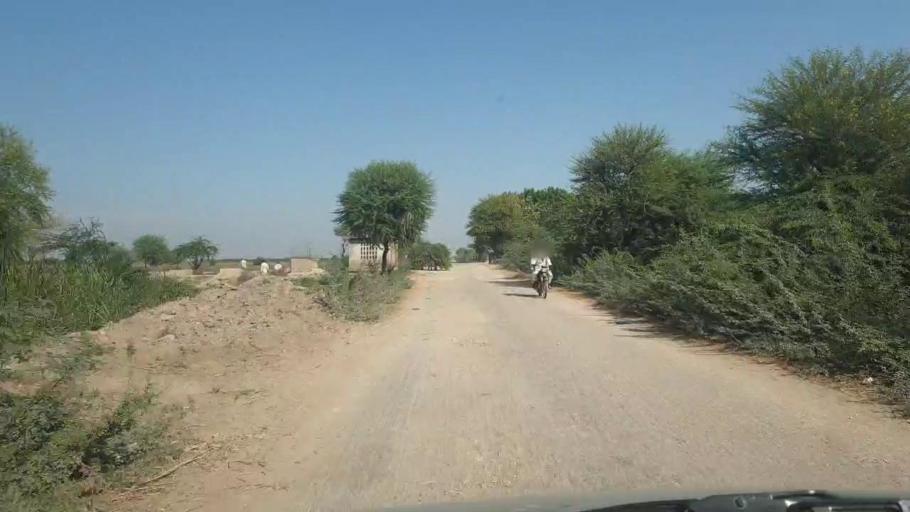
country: PK
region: Sindh
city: Tando Bago
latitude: 24.8198
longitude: 68.9850
